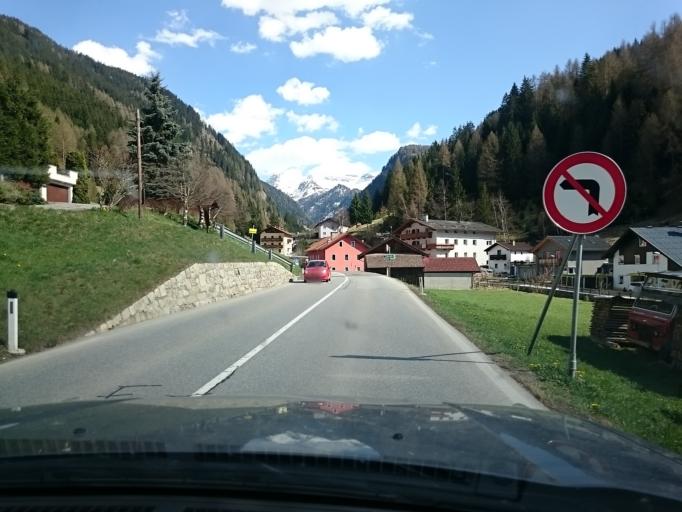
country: AT
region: Tyrol
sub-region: Politischer Bezirk Innsbruck Land
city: Gries am Brenner
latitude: 47.0362
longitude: 11.4804
